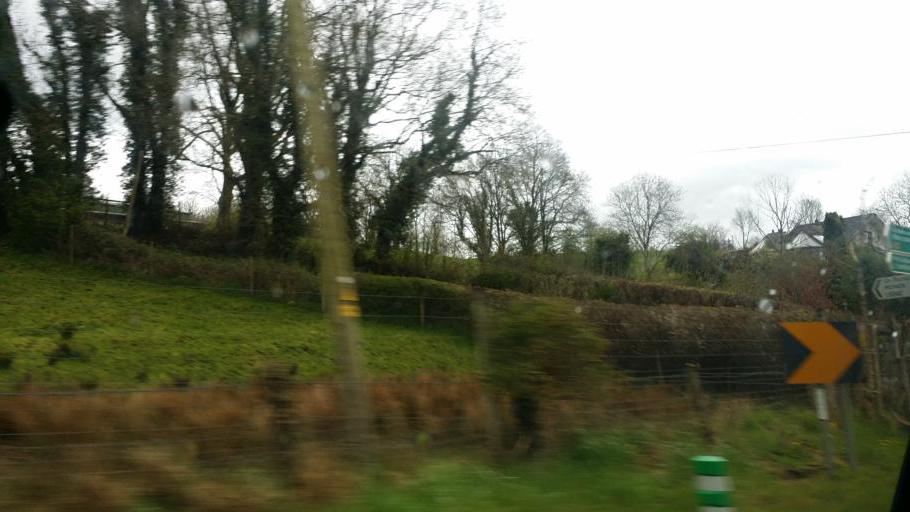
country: IE
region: Ulster
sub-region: An Cabhan
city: Ballyconnell
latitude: 54.1148
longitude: -7.6237
